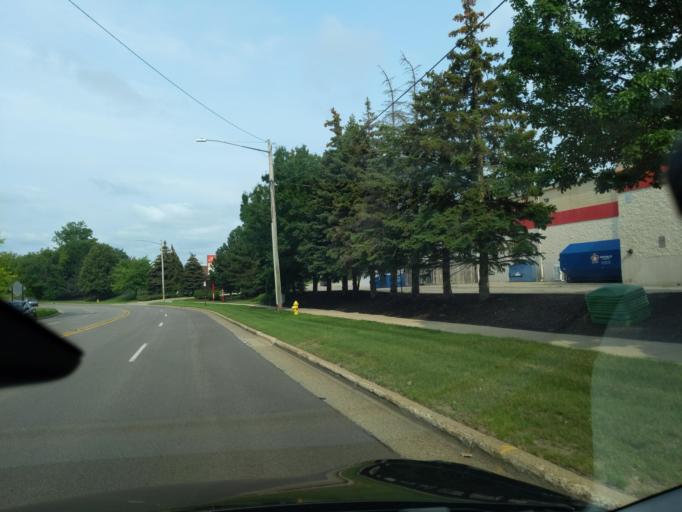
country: US
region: Michigan
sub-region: Kent County
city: East Grand Rapids
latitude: 42.9106
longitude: -85.5700
